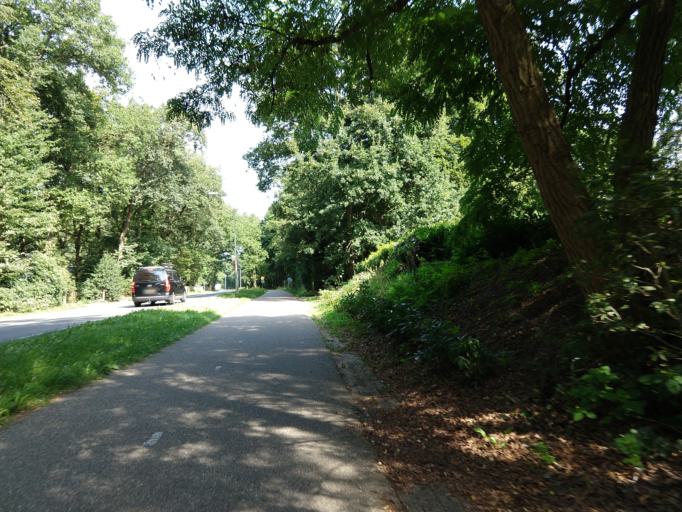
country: NL
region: Gelderland
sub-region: Gemeente Ede
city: Otterlo
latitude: 52.1074
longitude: 5.7688
